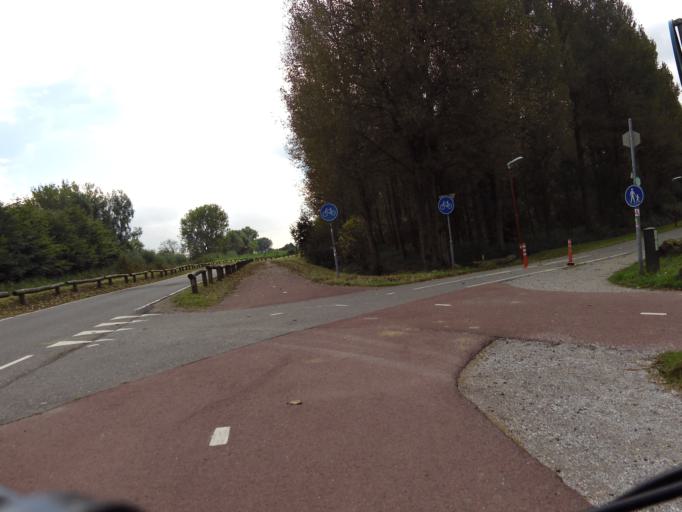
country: NL
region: South Holland
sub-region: Gemeente Zoetermeer
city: Zoetermeer
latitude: 52.0923
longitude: 4.5053
